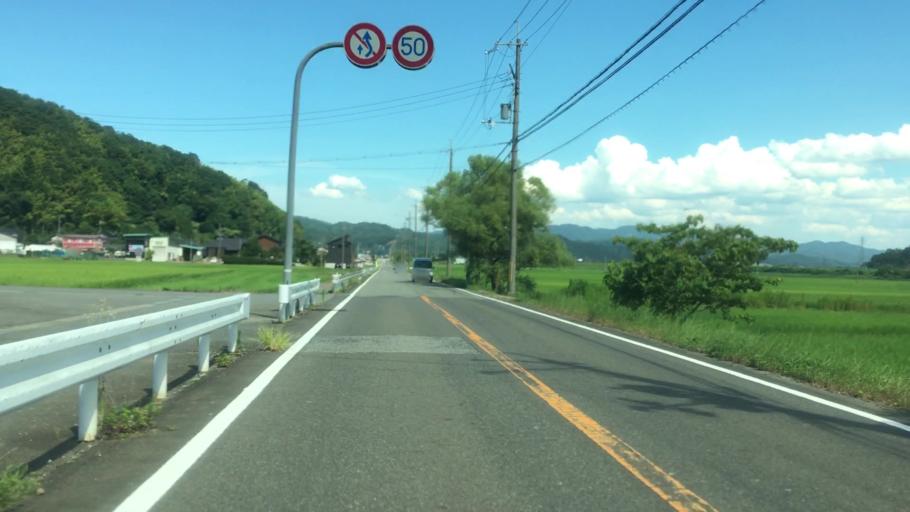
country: JP
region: Hyogo
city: Toyooka
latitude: 35.5671
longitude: 134.7929
